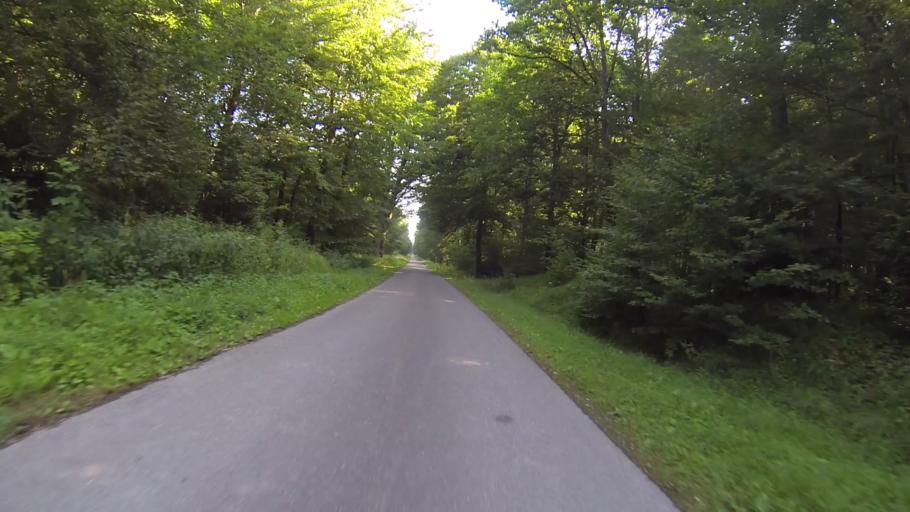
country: DE
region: Baden-Wuerttemberg
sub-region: Regierungsbezirk Stuttgart
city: Konigsbronn
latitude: 48.7166
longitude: 10.1117
